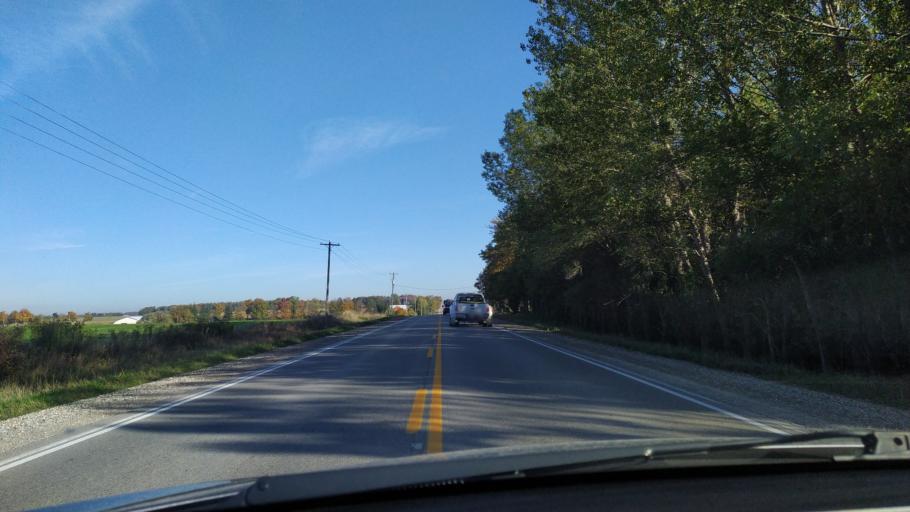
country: CA
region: Ontario
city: Stratford
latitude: 43.4557
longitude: -80.8390
